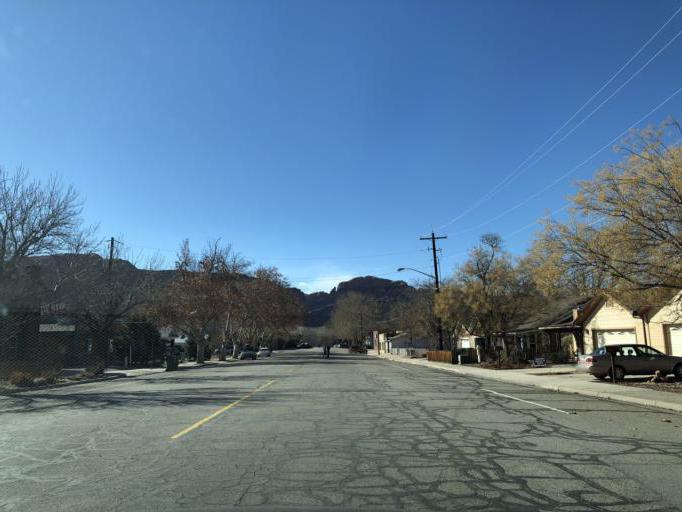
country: US
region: Utah
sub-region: Grand County
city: Moab
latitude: 38.5718
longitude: -109.5468
